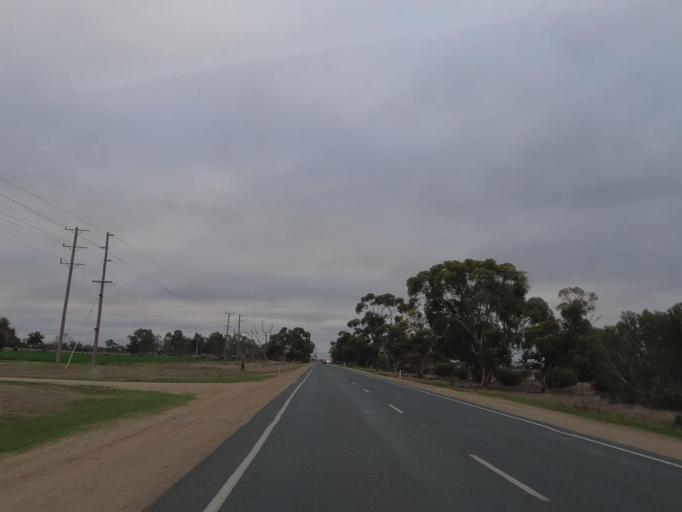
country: AU
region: Victoria
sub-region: Swan Hill
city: Swan Hill
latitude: -35.3993
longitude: 143.5760
